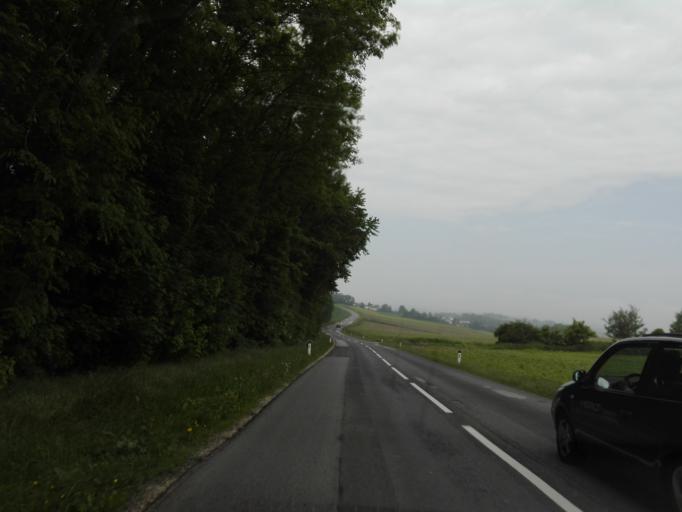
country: AT
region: Upper Austria
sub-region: Politischer Bezirk Linz-Land
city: Pasching
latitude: 48.2747
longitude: 14.1793
